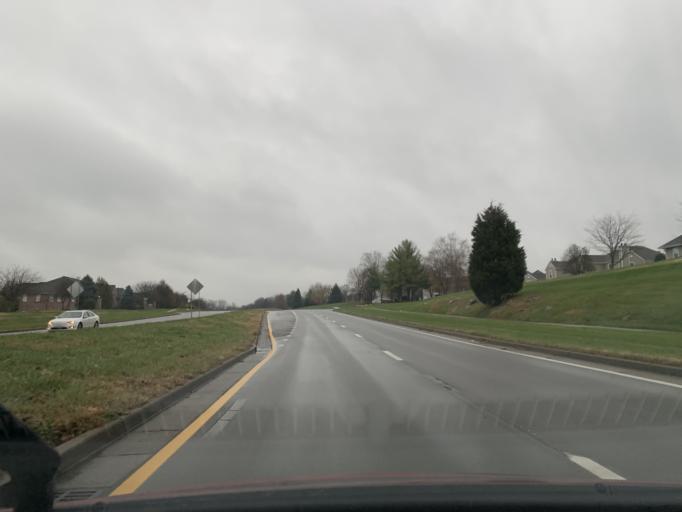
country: US
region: Kentucky
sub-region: Jefferson County
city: Hurstbourne Acres
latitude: 38.1996
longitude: -85.6028
